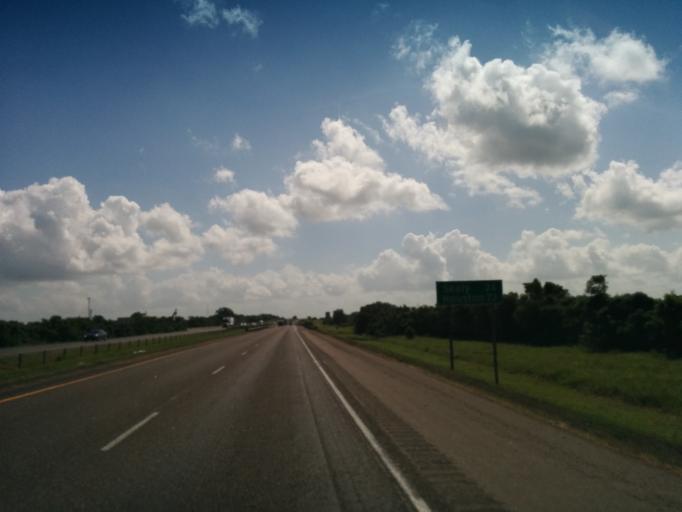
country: US
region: Texas
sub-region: Colorado County
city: Columbus
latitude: 29.6991
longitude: -96.5275
